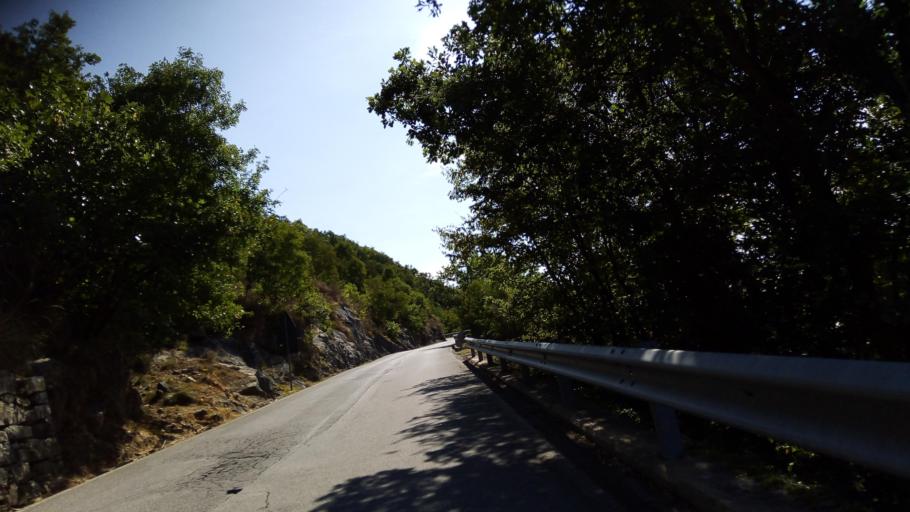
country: IT
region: Liguria
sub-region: Provincia di Savona
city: Balestrino
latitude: 44.1447
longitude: 8.1664
